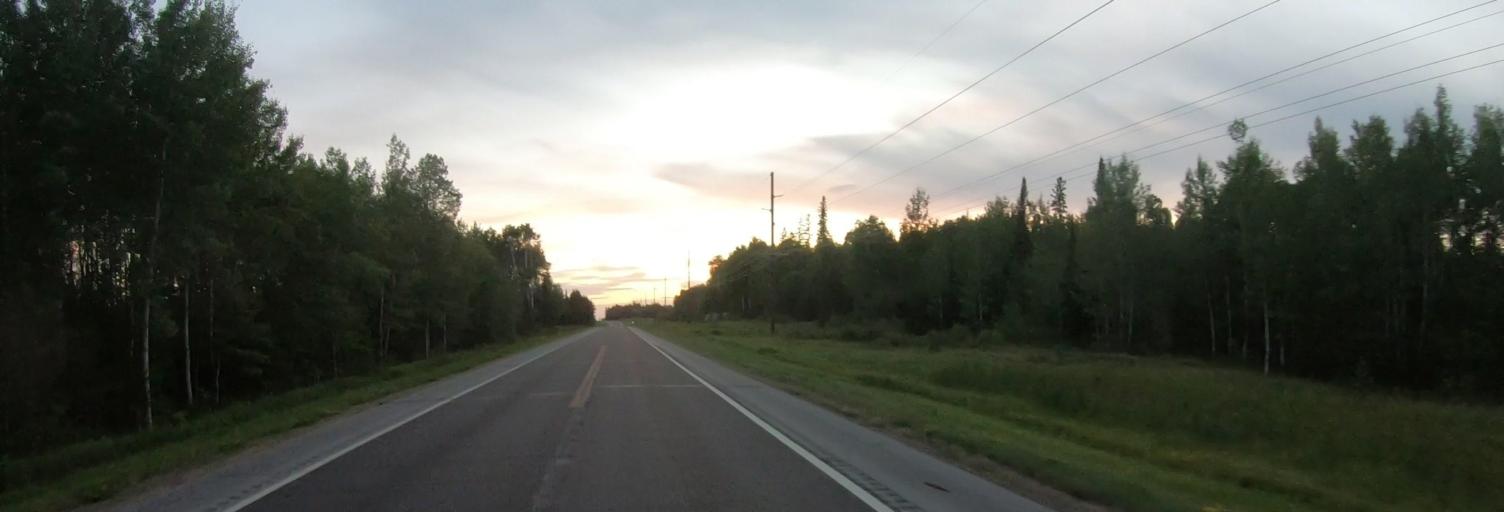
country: US
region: Minnesota
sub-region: Saint Louis County
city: Parkville
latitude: 47.8464
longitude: -92.5413
